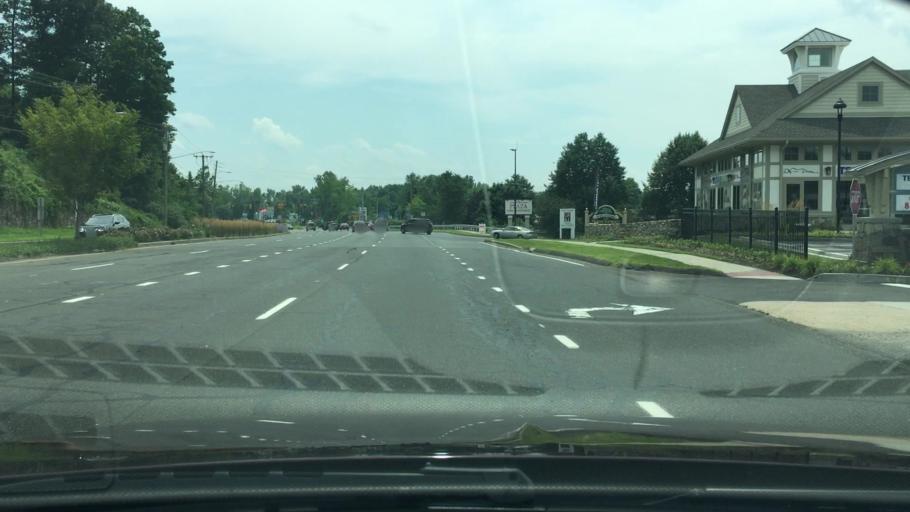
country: US
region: Connecticut
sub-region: Hartford County
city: Manchester
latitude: 41.8082
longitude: -72.5554
